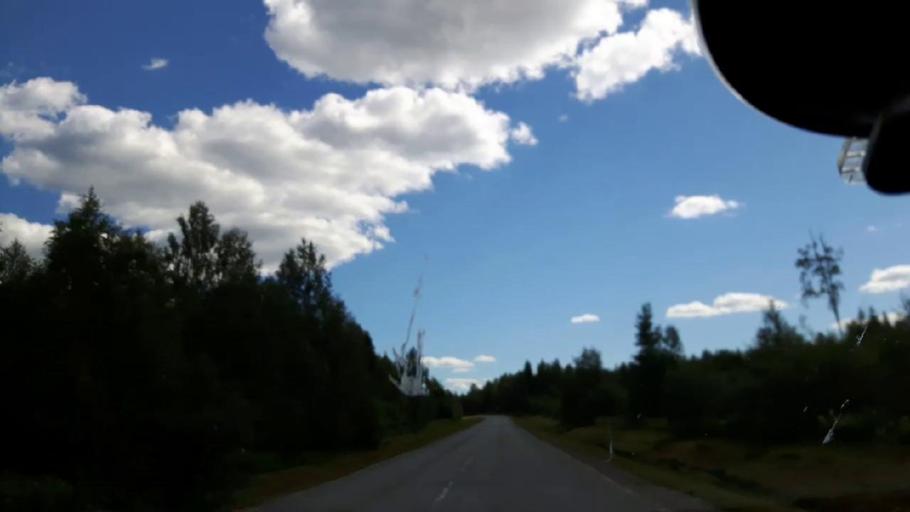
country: SE
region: Jaemtland
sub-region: Ragunda Kommun
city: Hammarstrand
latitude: 62.8291
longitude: 16.1856
